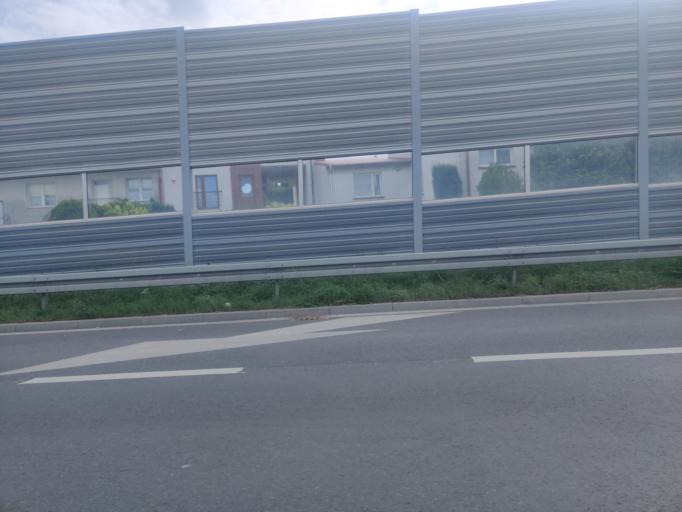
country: PL
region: Greater Poland Voivodeship
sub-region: Konin
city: Konin
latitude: 52.2025
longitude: 18.2750
